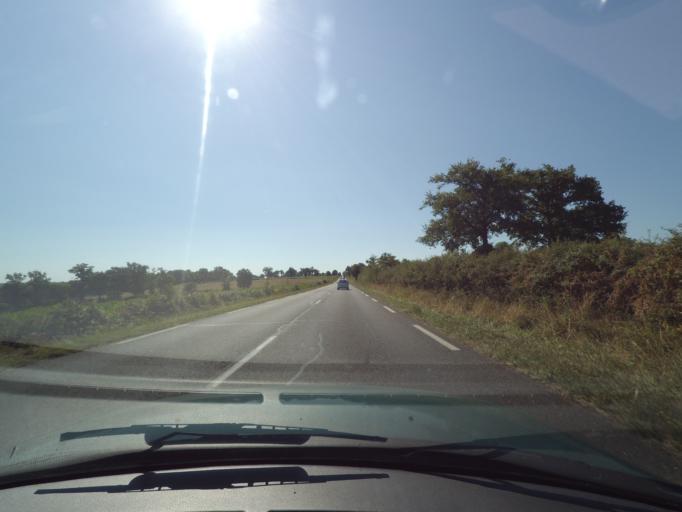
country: FR
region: Limousin
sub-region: Departement de la Haute-Vienne
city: Peyrat-de-Bellac
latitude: 46.1435
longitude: 0.9742
